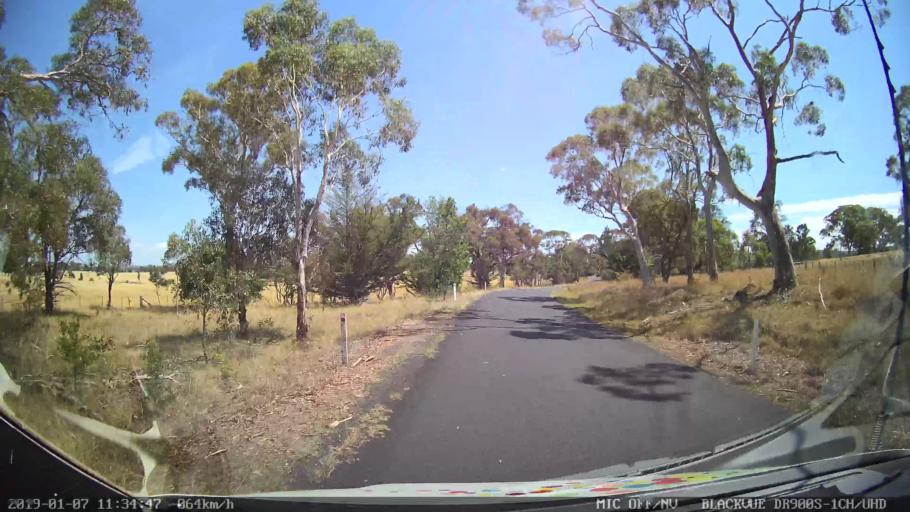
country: AU
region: New South Wales
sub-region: Armidale Dumaresq
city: Armidale
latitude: -30.3868
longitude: 151.5576
